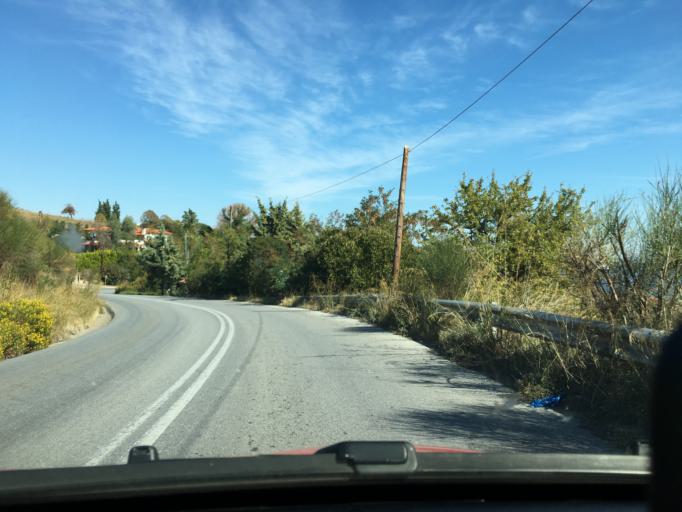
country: GR
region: Central Macedonia
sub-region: Nomos Chalkidikis
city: Nea Roda
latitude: 40.3795
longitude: 23.9114
